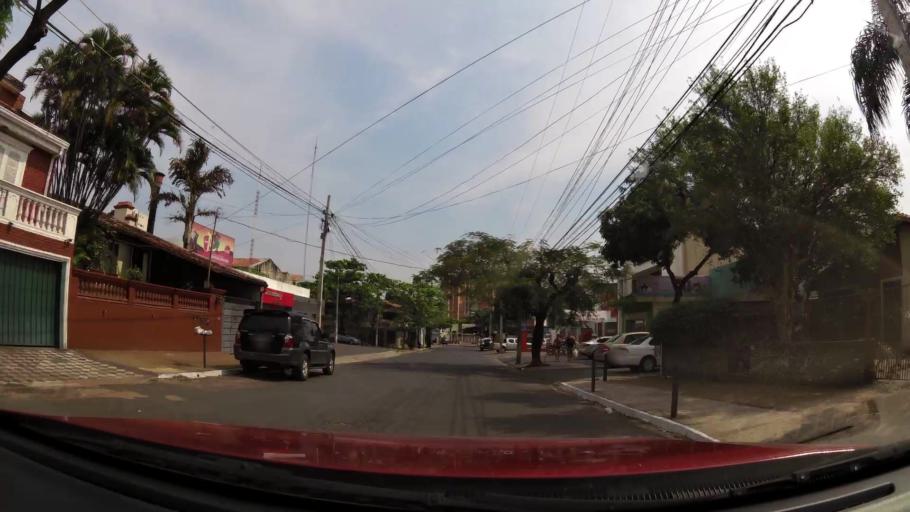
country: PY
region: Asuncion
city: Asuncion
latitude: -25.2744
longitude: -57.5667
